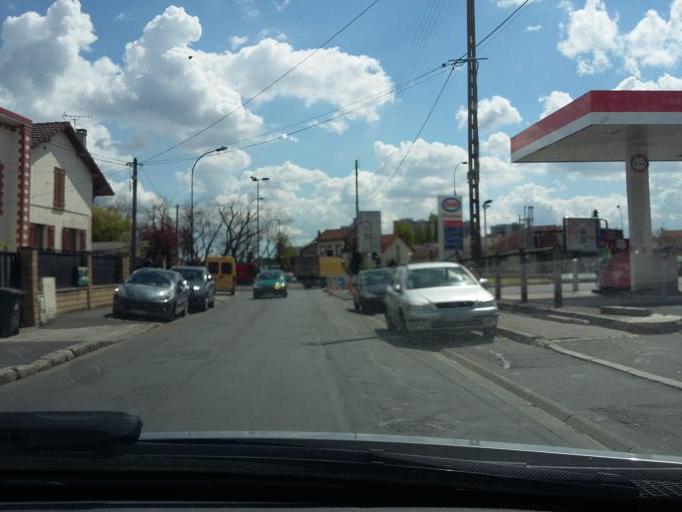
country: FR
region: Ile-de-France
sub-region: Departement de Seine-Saint-Denis
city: Epinay-sur-Seine
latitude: 48.9602
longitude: 2.3036
